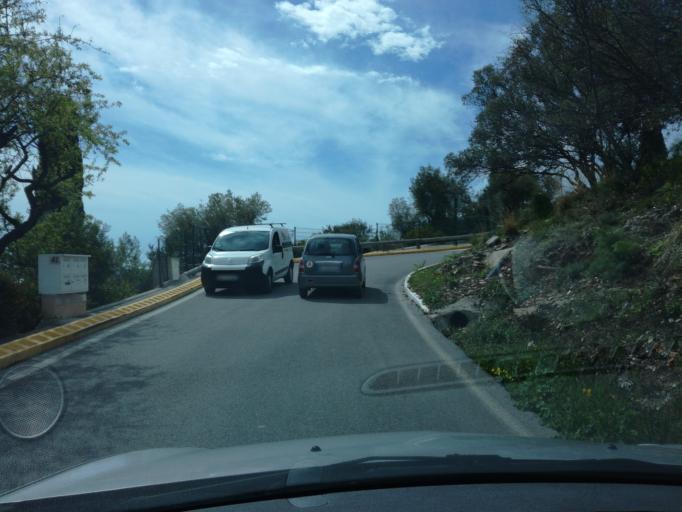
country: FR
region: Provence-Alpes-Cote d'Azur
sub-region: Departement du Var
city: Hyeres
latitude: 43.1240
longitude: 6.1288
